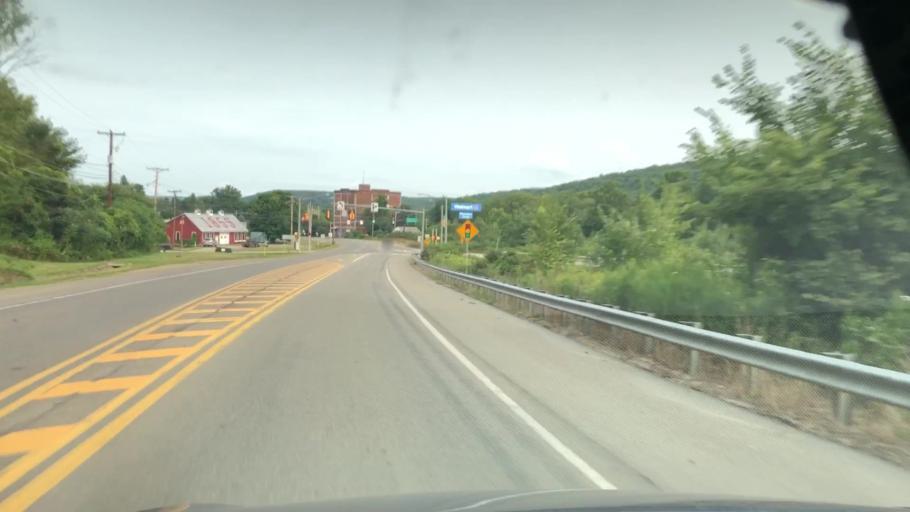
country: US
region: Pennsylvania
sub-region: Crawford County
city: Titusville
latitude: 41.6341
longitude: -79.6968
